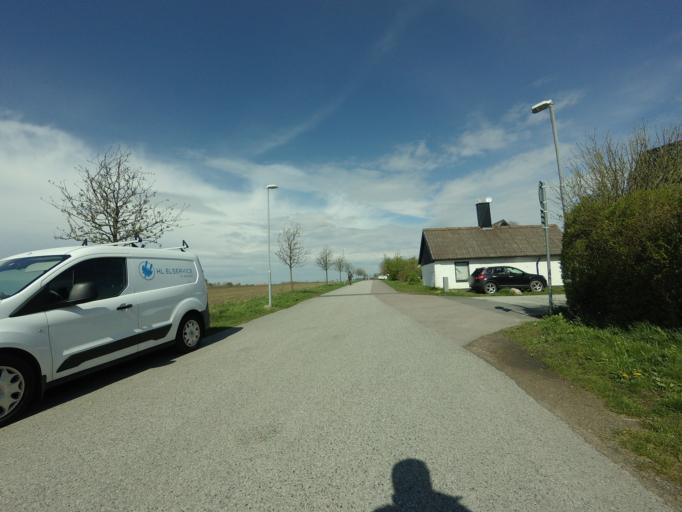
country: SE
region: Skane
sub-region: Vellinge Kommun
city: Vellinge
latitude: 55.4891
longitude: 13.0087
